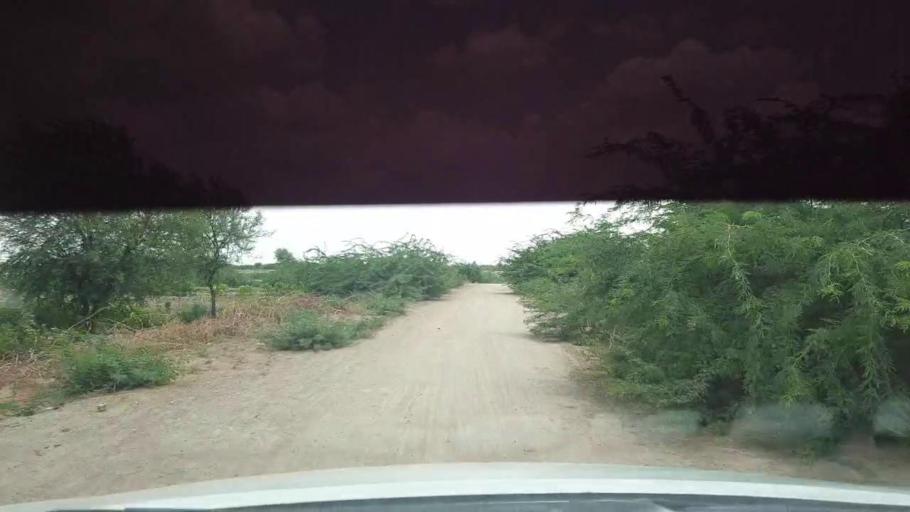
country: PK
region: Sindh
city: Kadhan
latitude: 24.5240
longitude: 69.0855
